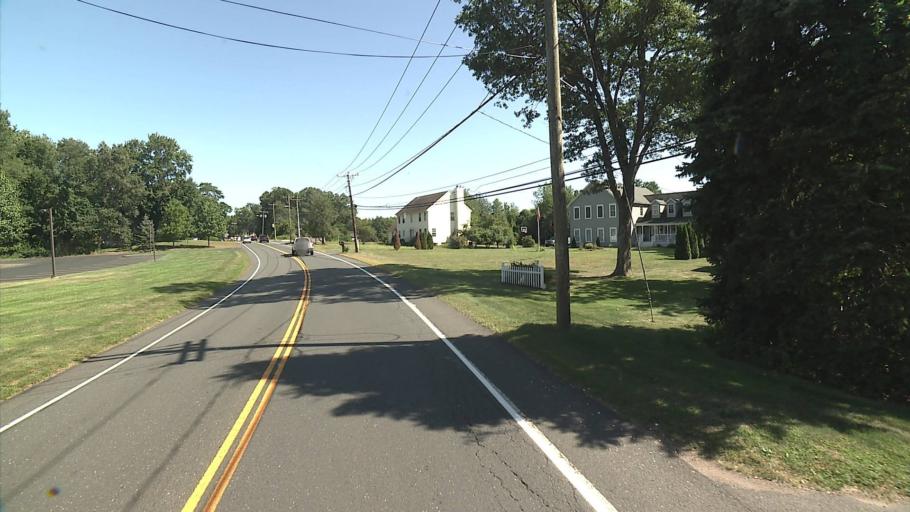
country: US
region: Connecticut
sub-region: Hartford County
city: Blue Hills
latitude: 41.8367
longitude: -72.6816
